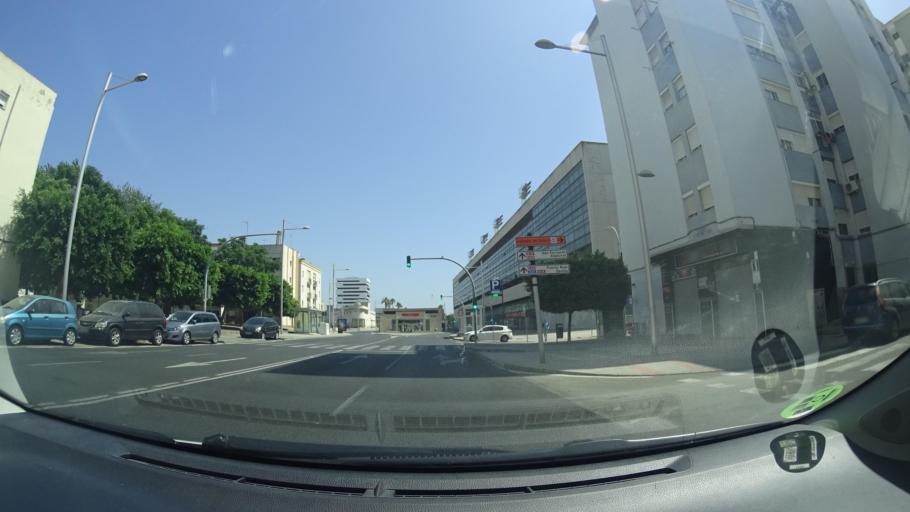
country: ES
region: Andalusia
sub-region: Provincia de Cadiz
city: Cadiz
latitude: 36.5041
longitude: -6.2727
